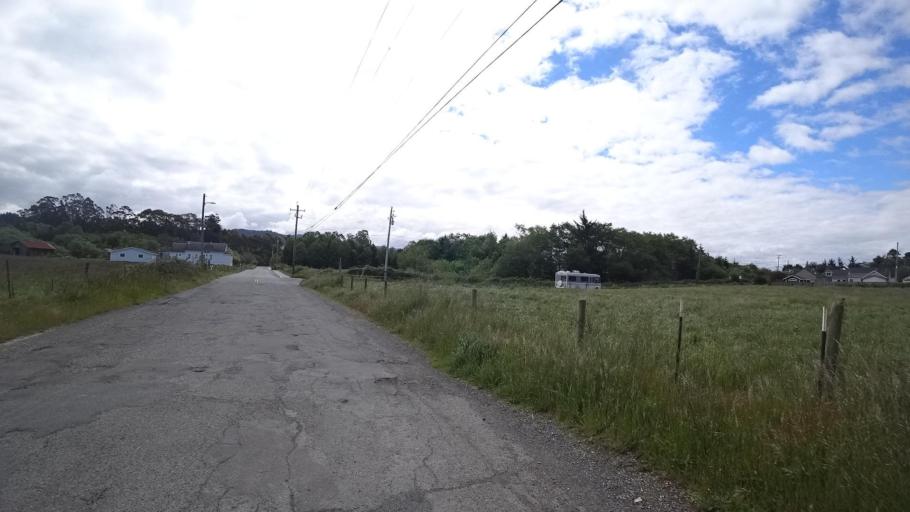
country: US
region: California
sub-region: Humboldt County
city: Arcata
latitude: 40.8777
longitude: -124.0947
